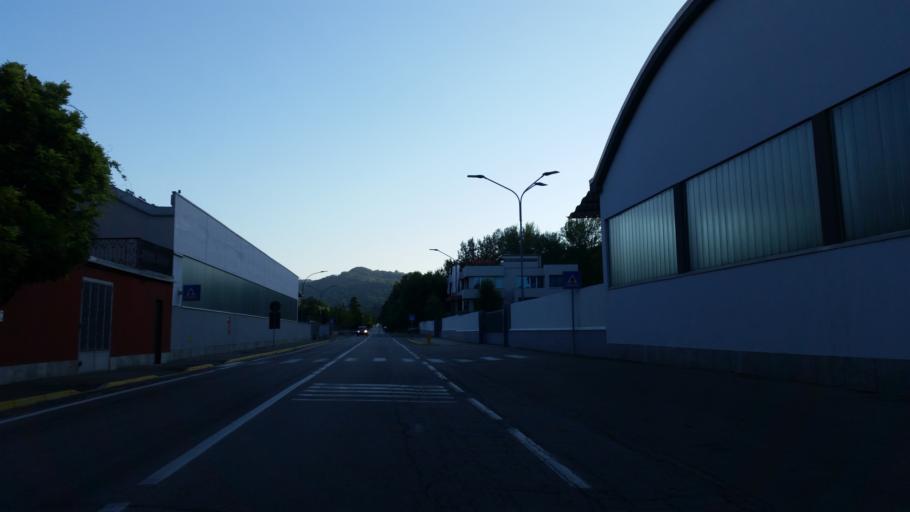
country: IT
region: Piedmont
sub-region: Provincia di Cuneo
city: Santo Stefano Belbo
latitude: 44.7007
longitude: 8.2188
